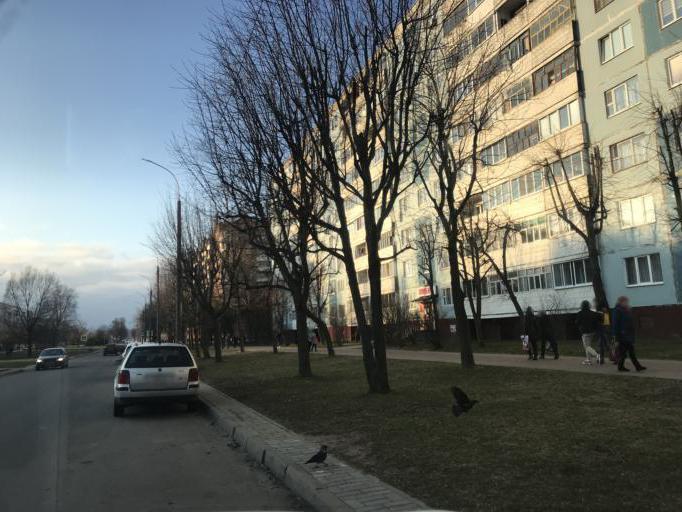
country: BY
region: Mogilev
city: Mahilyow
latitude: 53.8723
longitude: 30.3356
